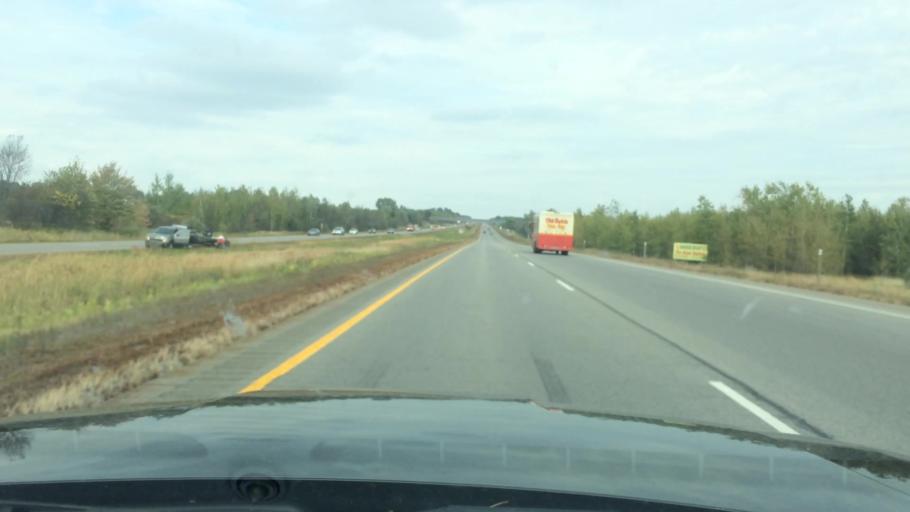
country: US
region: Wisconsin
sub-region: Marathon County
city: Mosinee
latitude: 44.7344
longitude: -89.6796
